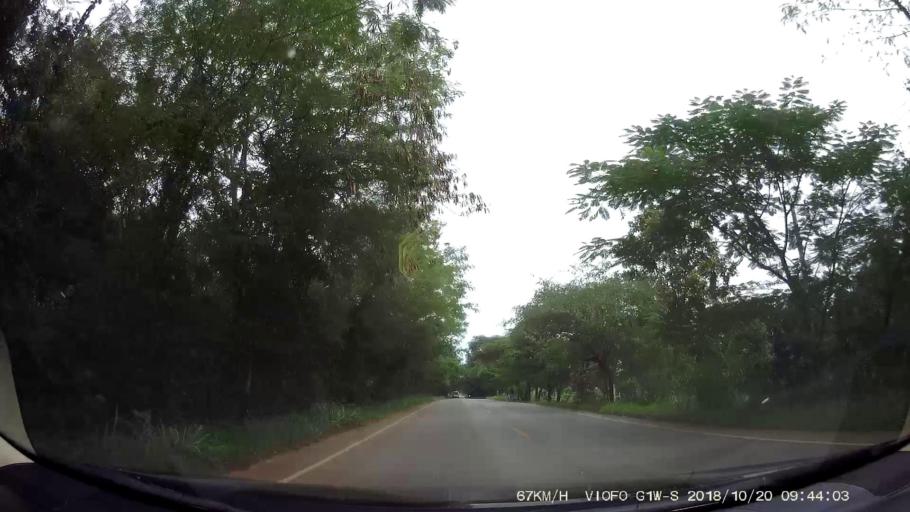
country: TH
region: Chaiyaphum
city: Khon San
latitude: 16.4793
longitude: 101.9456
